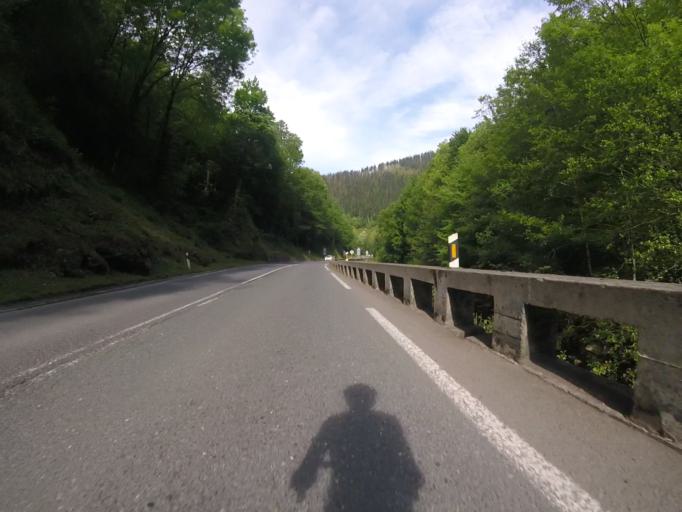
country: ES
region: Basque Country
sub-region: Provincia de Guipuzcoa
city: Urretxu
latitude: 43.1138
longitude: -2.3280
